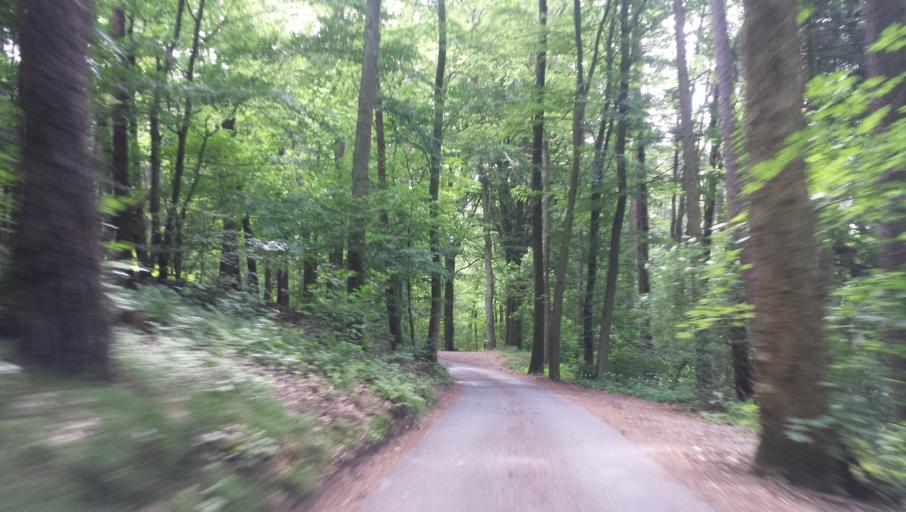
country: DE
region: Hesse
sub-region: Regierungsbezirk Darmstadt
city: Wald-Michelbach
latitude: 49.6143
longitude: 8.8363
